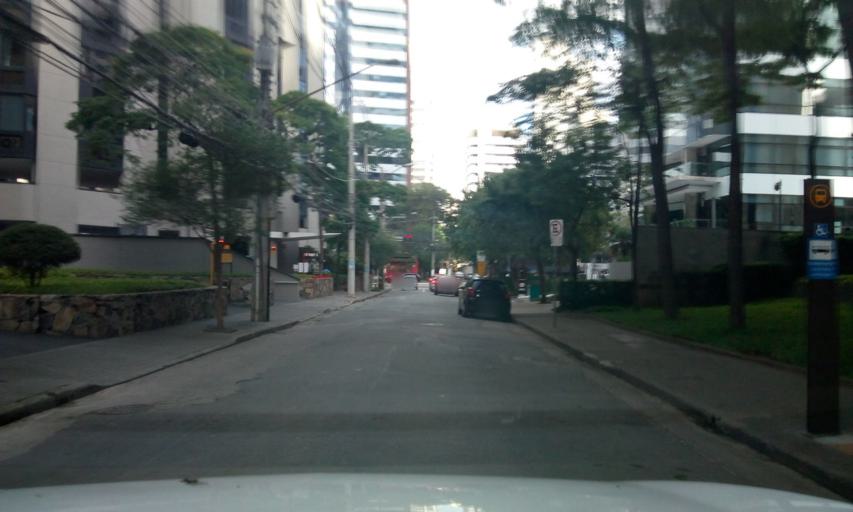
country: BR
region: Sao Paulo
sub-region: Sao Paulo
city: Sao Paulo
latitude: -23.6079
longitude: -46.6950
